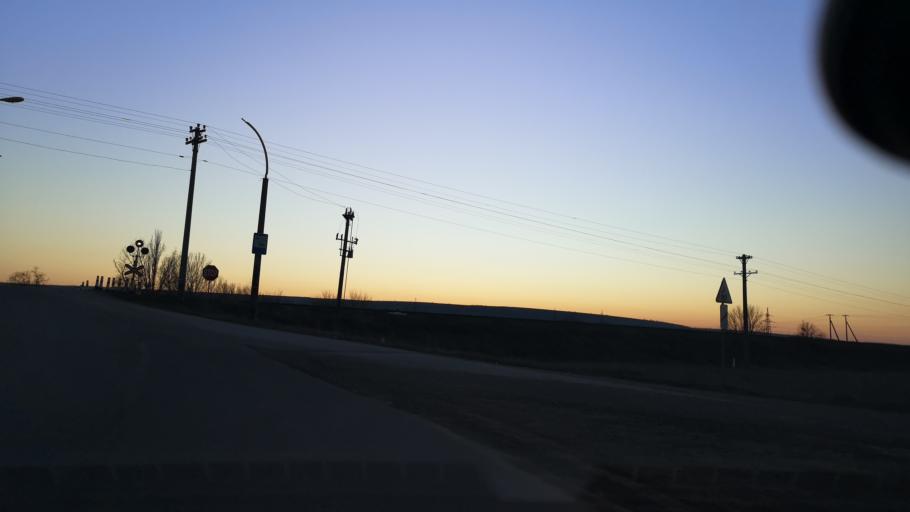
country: MD
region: Anenii Noi
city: Anenii Noi
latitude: 46.8912
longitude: 29.2417
